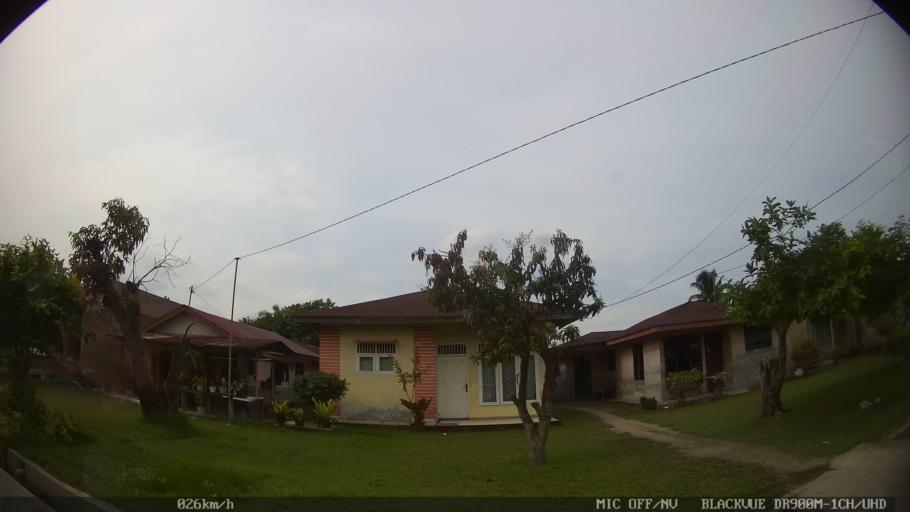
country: ID
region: North Sumatra
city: Medan
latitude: 3.5694
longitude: 98.7564
